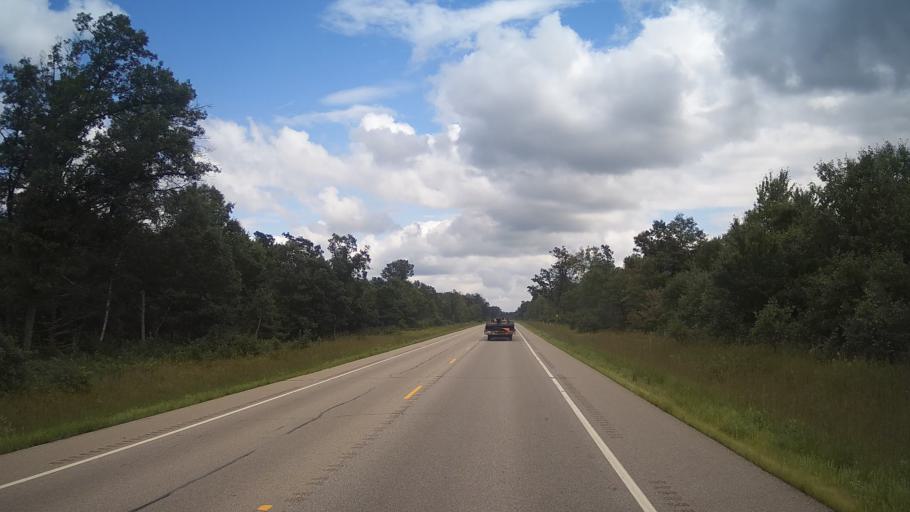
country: US
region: Wisconsin
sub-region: Adams County
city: Friendship
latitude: 44.0256
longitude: -89.7061
